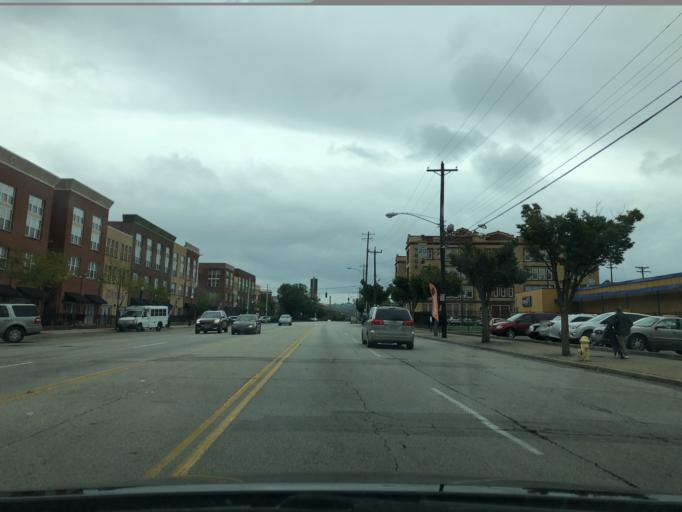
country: US
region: Kentucky
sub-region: Kenton County
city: Ludlow
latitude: 39.1126
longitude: -84.5276
